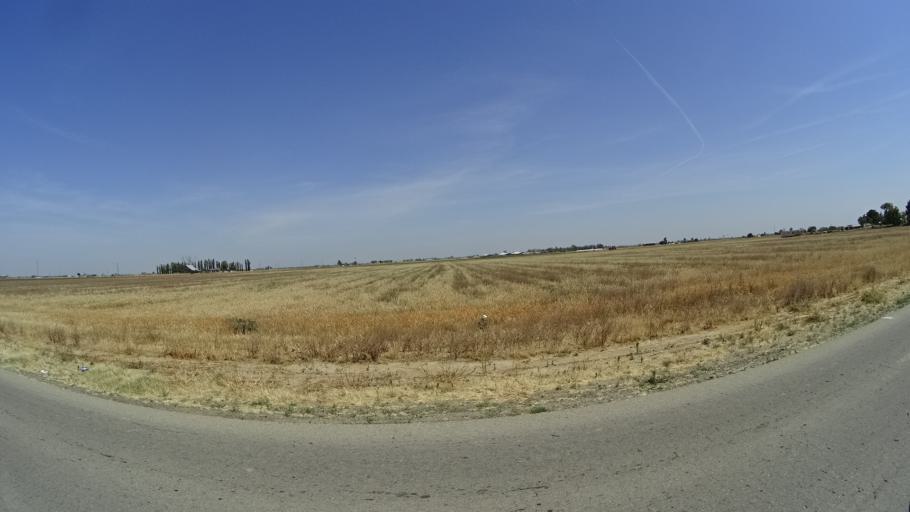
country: US
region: California
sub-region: Fresno County
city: Riverdale
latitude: 36.4019
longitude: -119.8668
